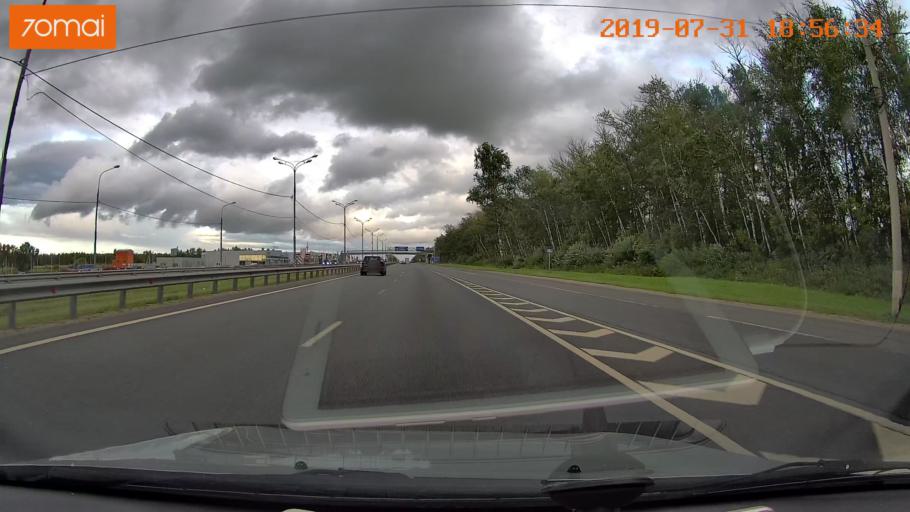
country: RU
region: Moskovskaya
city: Raduzhnyy
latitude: 55.1619
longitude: 38.6797
